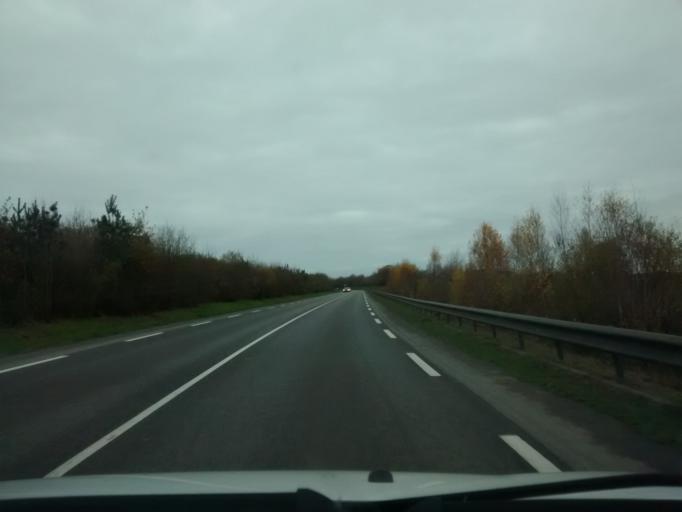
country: FR
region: Brittany
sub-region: Departement d'Ille-et-Vilaine
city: Etrelles
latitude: 48.0650
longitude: -1.1856
